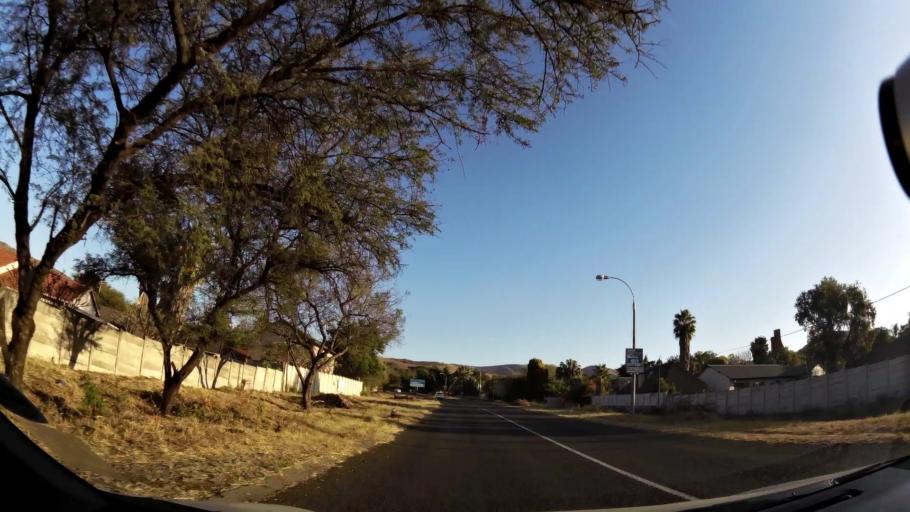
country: ZA
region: North-West
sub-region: Bojanala Platinum District Municipality
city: Rustenburg
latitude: -25.6964
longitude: 27.2193
